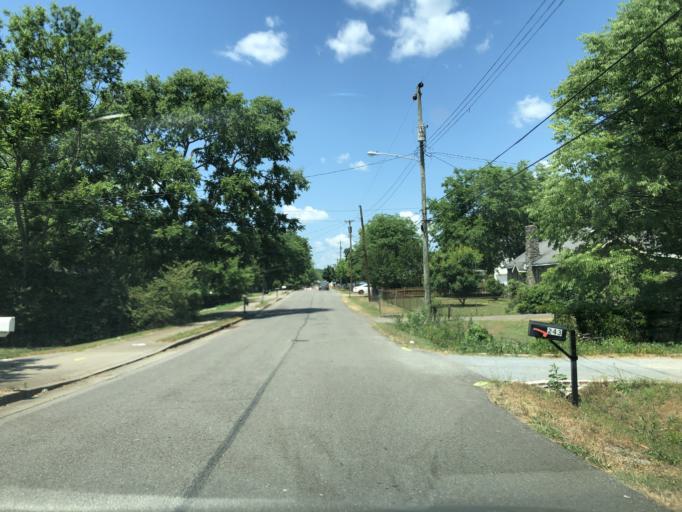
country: US
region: Tennessee
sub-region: Davidson County
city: Goodlettsville
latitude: 36.2666
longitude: -86.7075
